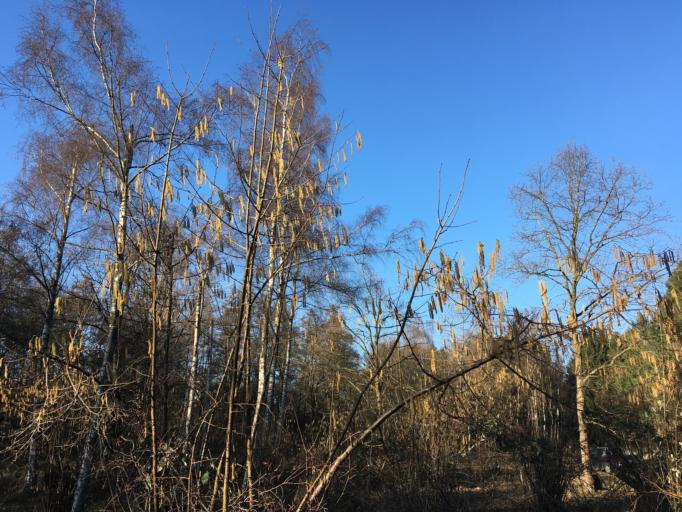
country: DK
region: Capital Region
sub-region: Ballerup Kommune
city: Ballerup
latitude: 55.7483
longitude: 12.3514
